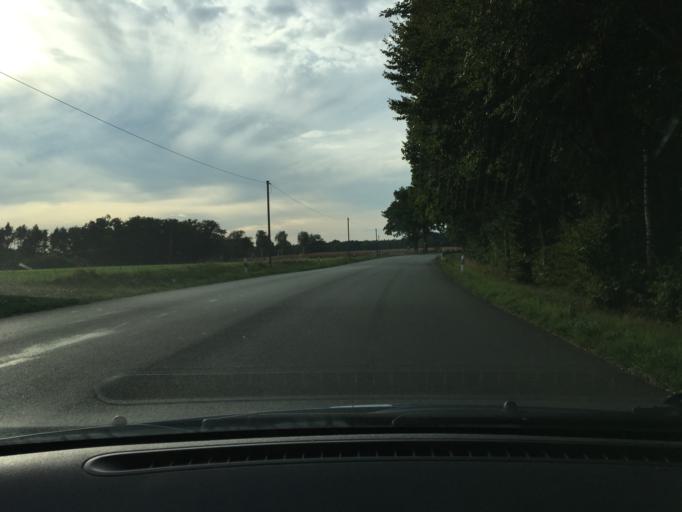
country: DE
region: Lower Saxony
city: Munster
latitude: 52.9182
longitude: 10.0672
